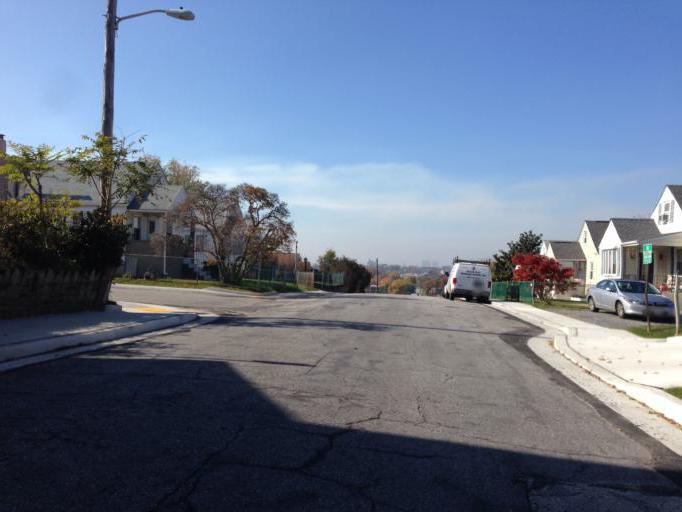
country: US
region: Maryland
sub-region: Baltimore County
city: Dundalk
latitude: 39.2850
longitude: -76.5237
